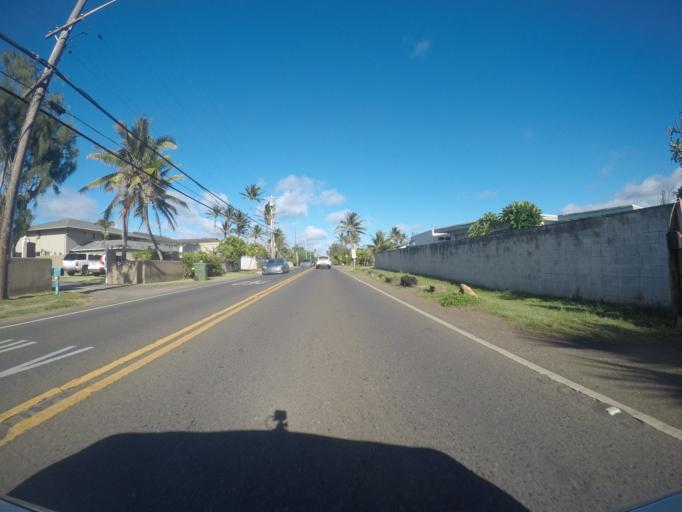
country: US
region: Hawaii
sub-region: Honolulu County
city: La'ie
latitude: 21.6516
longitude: -157.9276
